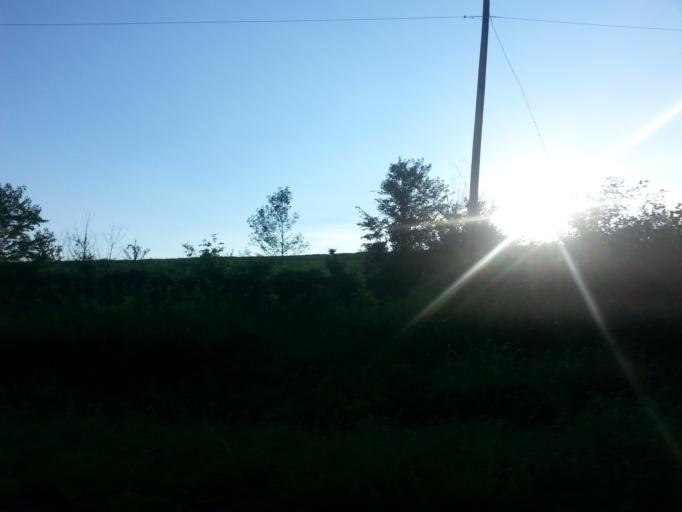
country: US
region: Tennessee
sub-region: Loudon County
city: Greenback
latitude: 35.6958
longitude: -84.2314
